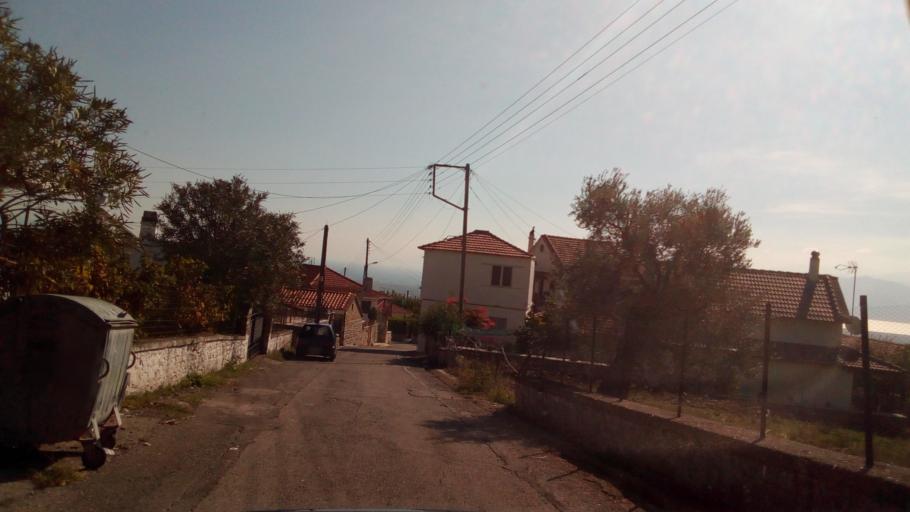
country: GR
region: West Greece
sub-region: Nomos Aitolias kai Akarnanias
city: Nafpaktos
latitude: 38.4228
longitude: 21.8637
